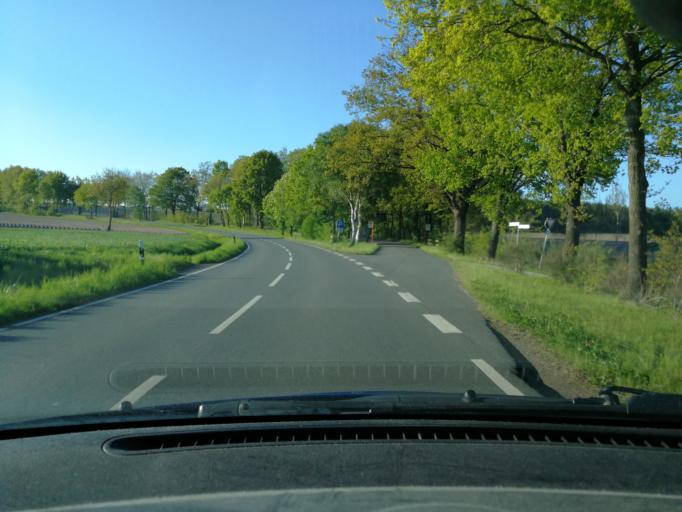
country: DE
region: Lower Saxony
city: Betzendorf
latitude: 53.1242
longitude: 10.3105
